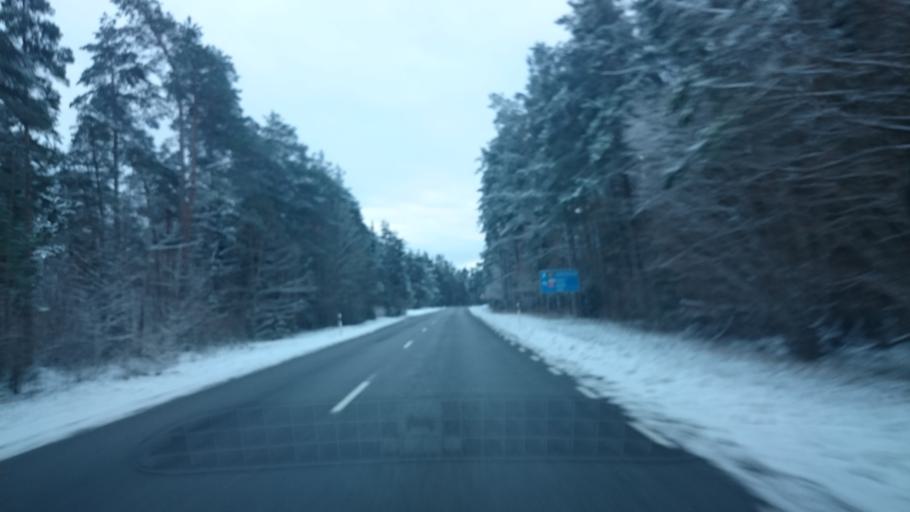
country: EE
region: Saare
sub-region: Kuressaare linn
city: Kuressaare
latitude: 58.3921
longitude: 22.6480
